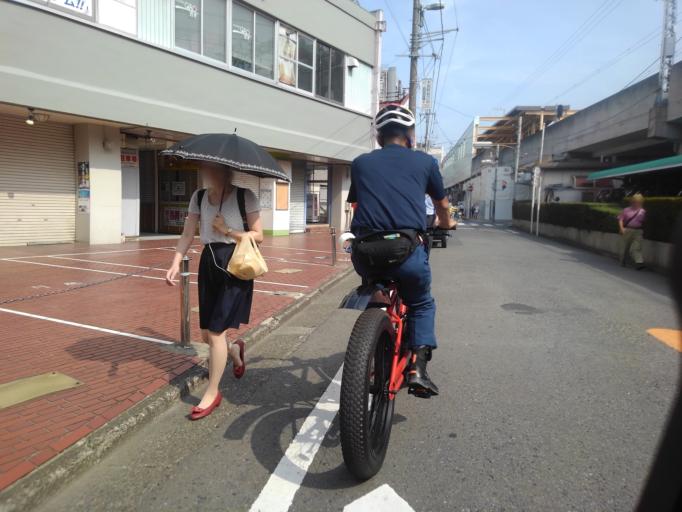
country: JP
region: Kanagawa
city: Minami-rinkan
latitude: 35.4682
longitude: 139.4621
